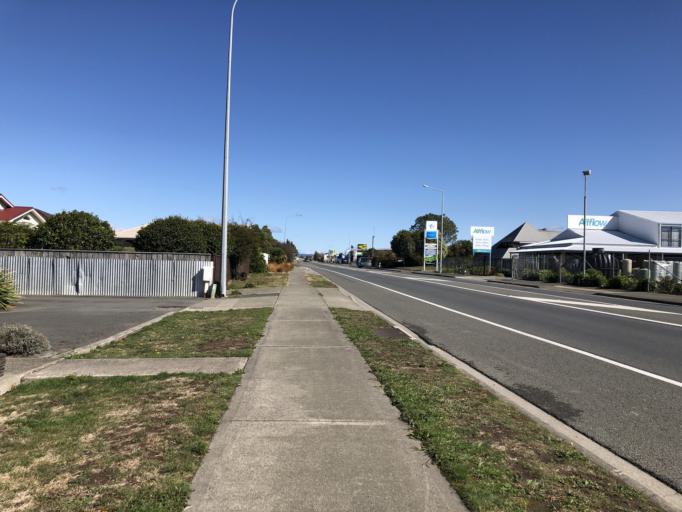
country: NZ
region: Tasman
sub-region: Tasman District
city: Richmond
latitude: -41.3429
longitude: 173.1719
